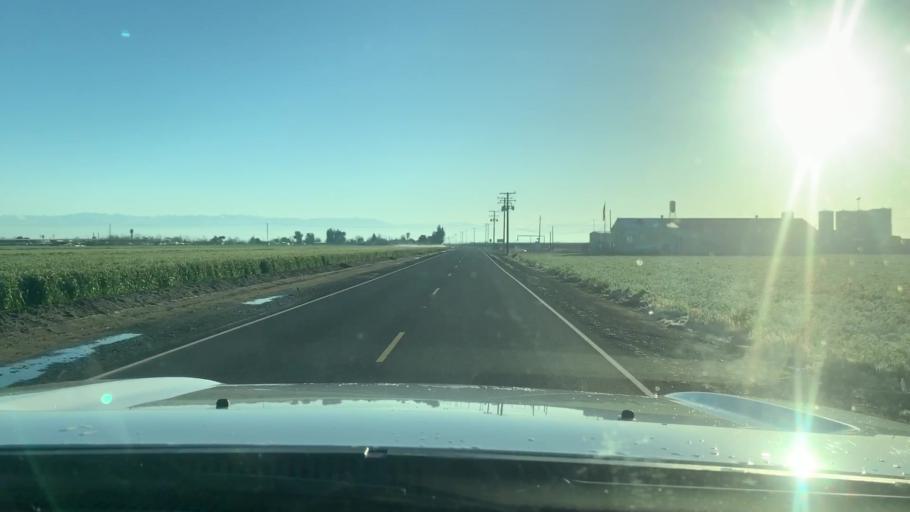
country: US
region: California
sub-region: Tulare County
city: Tulare
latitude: 36.2030
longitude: -119.4795
